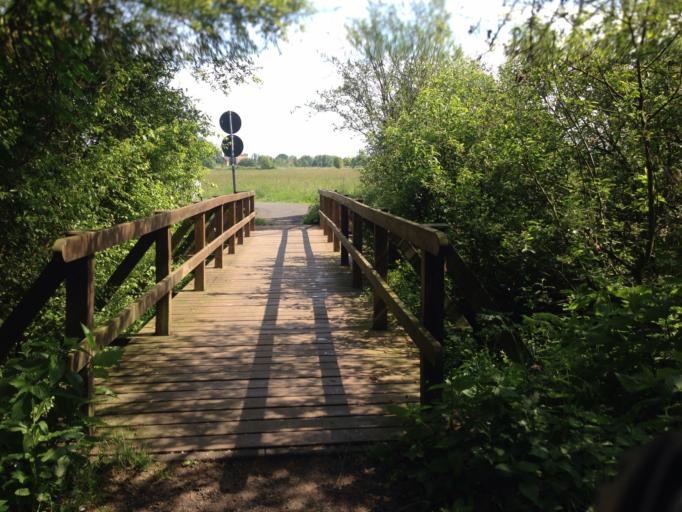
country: DE
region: Hesse
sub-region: Regierungsbezirk Darmstadt
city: Erlensee
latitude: 50.1493
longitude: 8.9906
